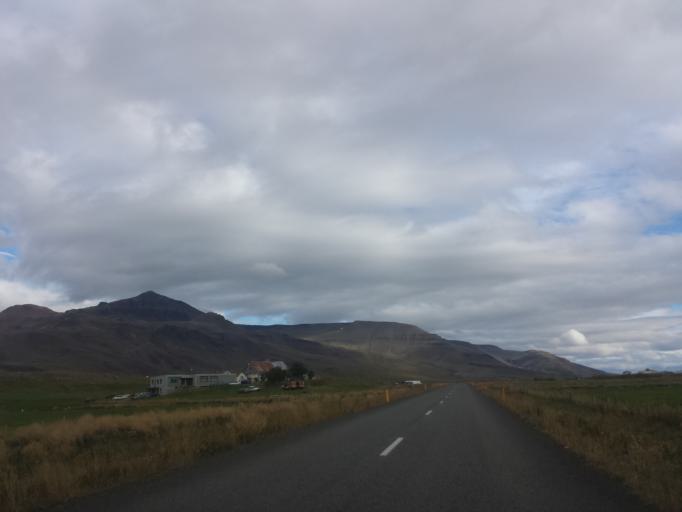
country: IS
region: West
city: Borgarnes
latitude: 64.4165
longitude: -21.8221
